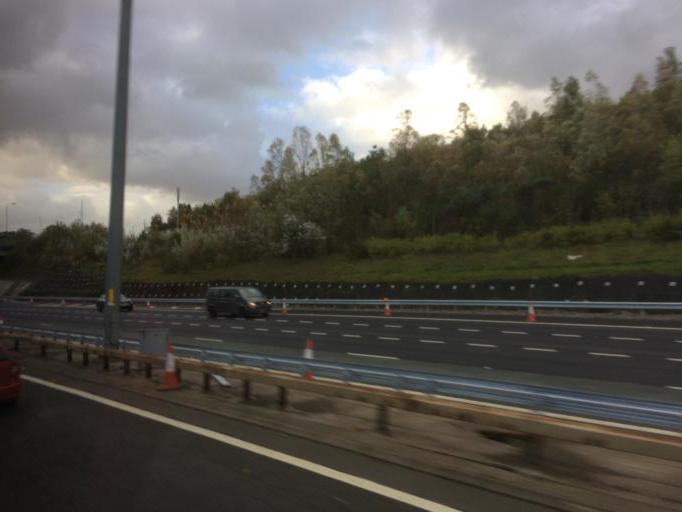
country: GB
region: Scotland
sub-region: North Lanarkshire
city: Chryston
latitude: 55.8612
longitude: -4.1057
